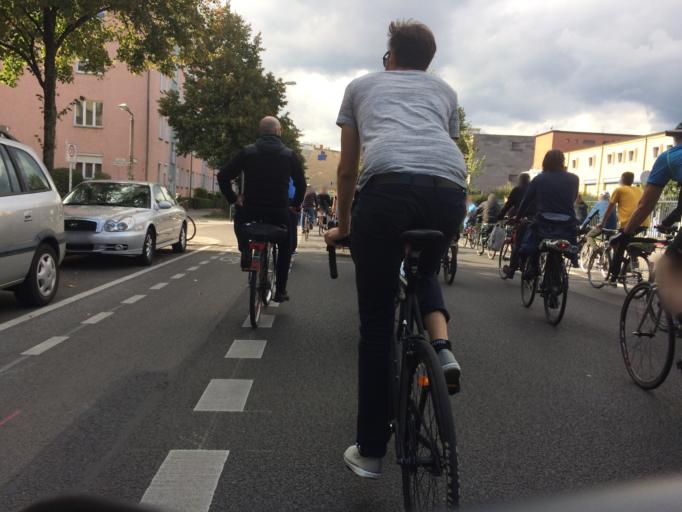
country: DE
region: Berlin
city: Friedrichshain Bezirk
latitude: 52.5208
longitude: 13.4573
